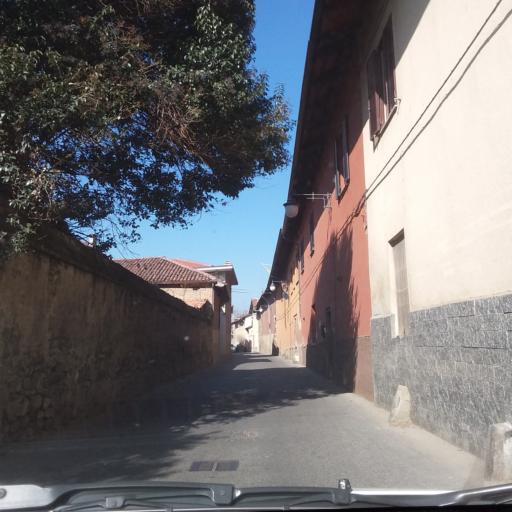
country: IT
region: Piedmont
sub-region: Provincia di Torino
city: Rivoli
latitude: 45.0650
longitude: 7.5167
